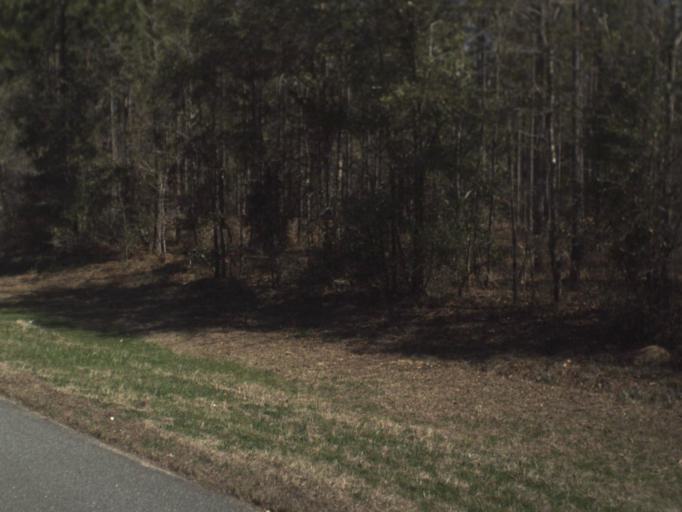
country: US
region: Florida
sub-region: Jackson County
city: Sneads
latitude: 30.6412
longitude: -85.0374
